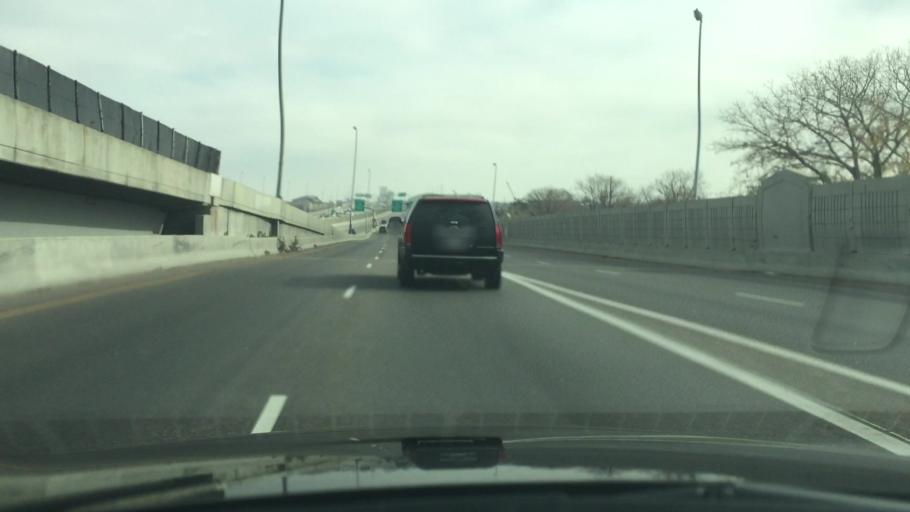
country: US
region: Colorado
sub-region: Denver County
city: Denver
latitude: 39.7795
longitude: -104.9859
